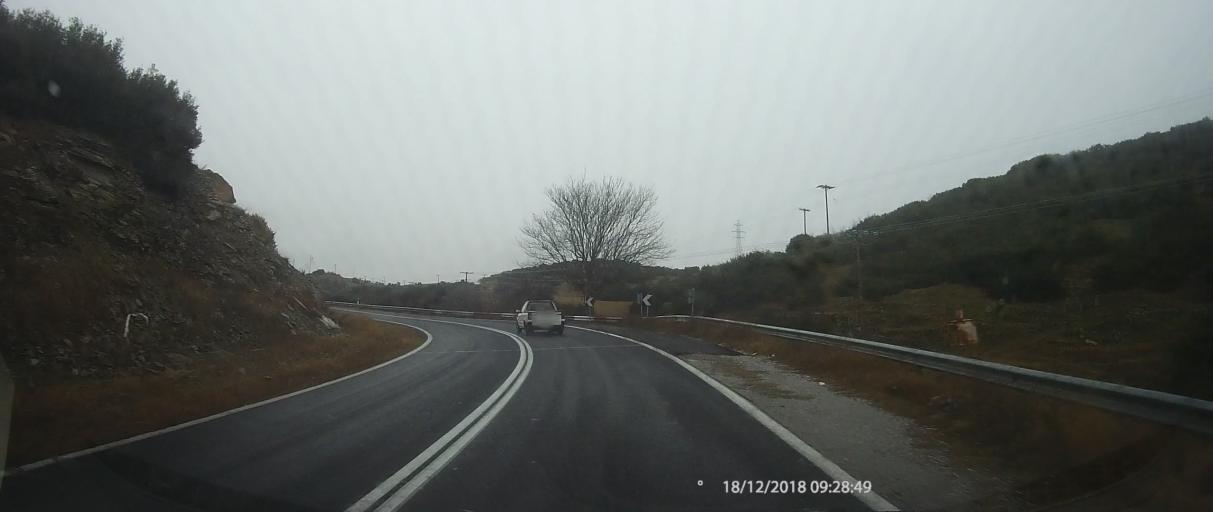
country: GR
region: Thessaly
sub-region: Nomos Larisis
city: Elassona
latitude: 39.9224
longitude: 22.1720
